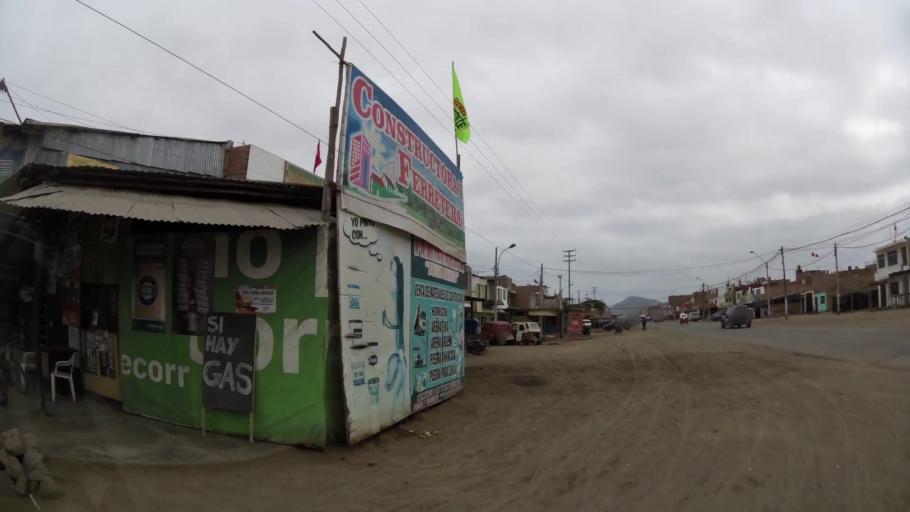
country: PE
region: Lima
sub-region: Provincia de Canete
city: Chilca
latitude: -12.5159
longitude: -76.7342
